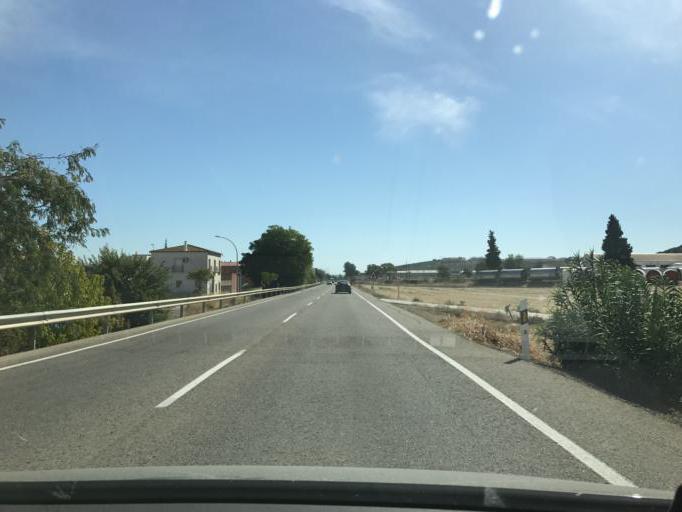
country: ES
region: Andalusia
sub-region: Province of Cordoba
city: Castro del Rio
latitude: 37.6844
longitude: -4.4810
